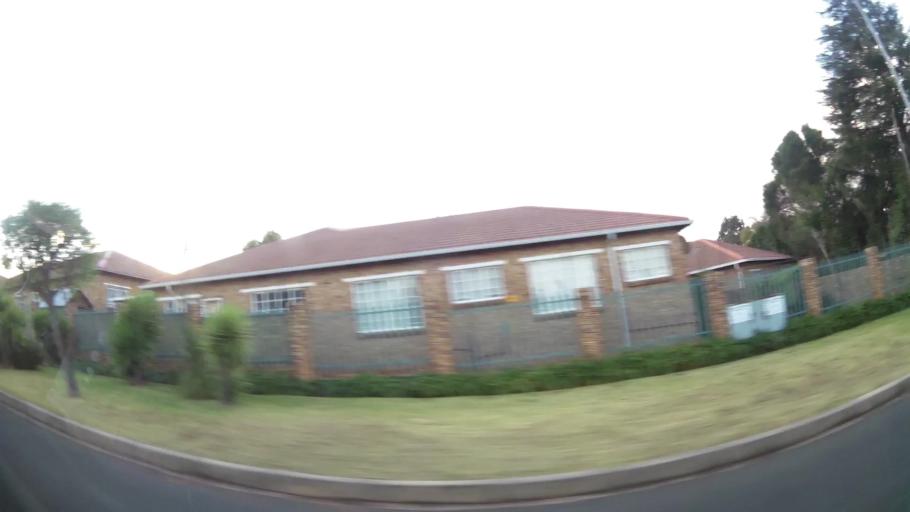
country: ZA
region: Gauteng
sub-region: West Rand District Municipality
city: Krugersdorp
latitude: -26.0698
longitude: 27.7934
